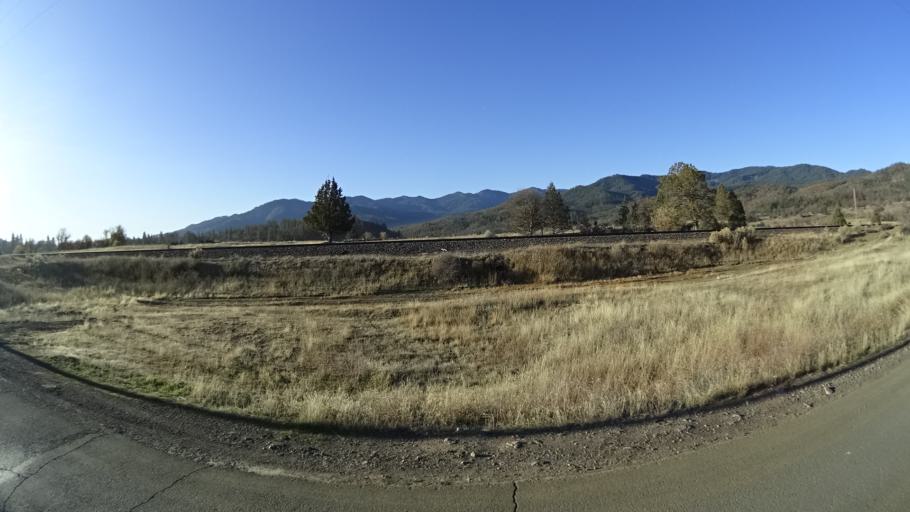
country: US
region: Oregon
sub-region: Jackson County
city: Ashland
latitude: 41.9985
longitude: -122.6315
